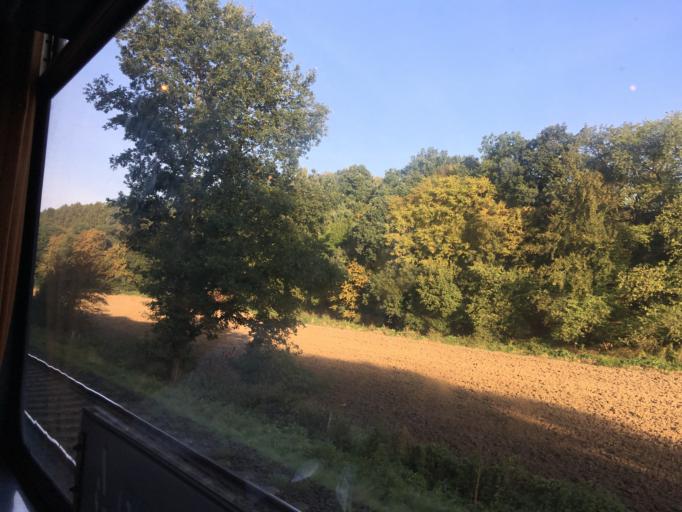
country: DE
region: North Rhine-Westphalia
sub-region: Regierungsbezirk Arnsberg
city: Frondenberg
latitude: 51.4725
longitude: 7.7418
